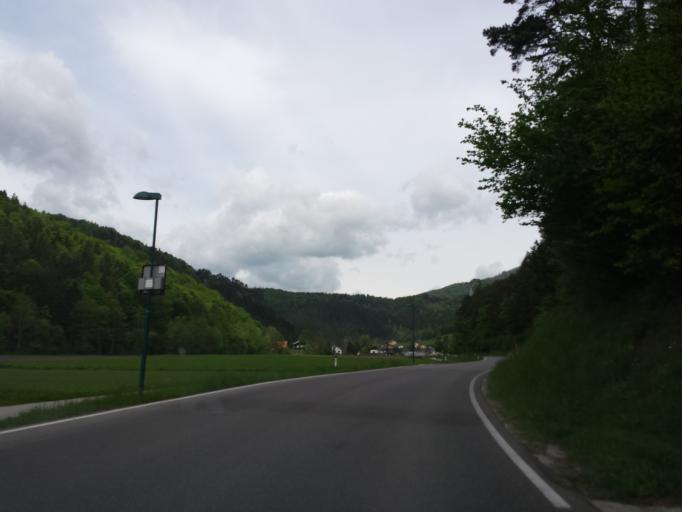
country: AT
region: Lower Austria
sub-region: Politischer Bezirk Wiener Neustadt
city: Pernitz
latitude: 47.9044
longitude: 15.9490
